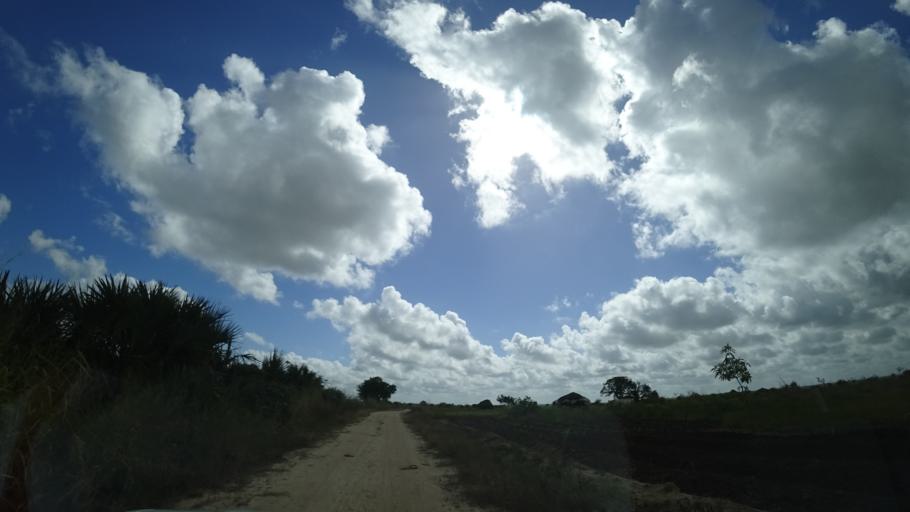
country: MZ
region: Sofala
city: Dondo
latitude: -19.4149
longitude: 34.5659
